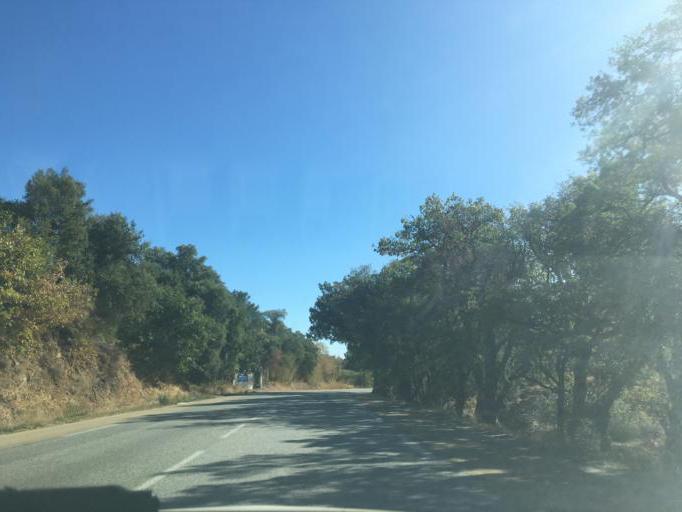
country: FR
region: Provence-Alpes-Cote d'Azur
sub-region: Departement du Var
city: Grimaud
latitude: 43.2876
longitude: 6.5002
